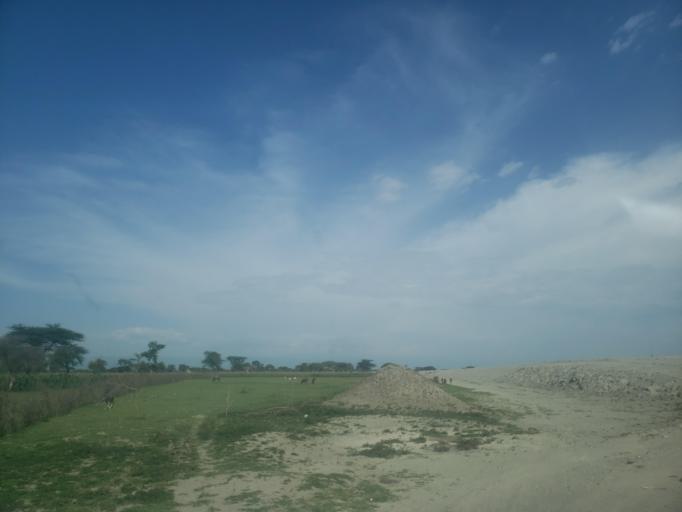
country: ET
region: Oromiya
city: Ziway
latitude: 7.6978
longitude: 38.6446
